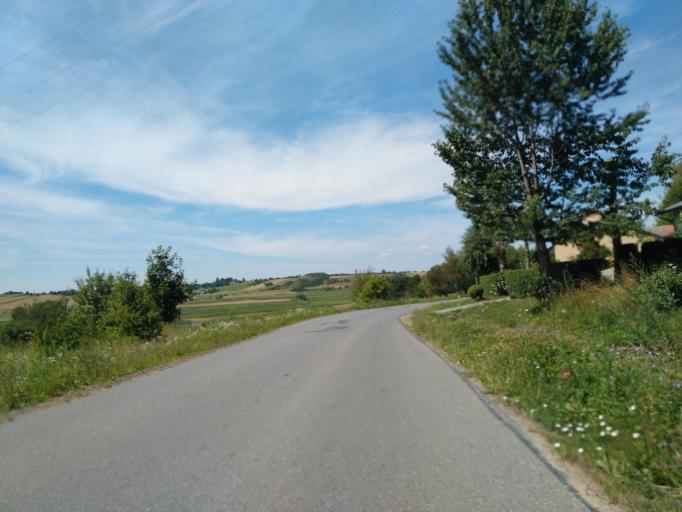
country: PL
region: Subcarpathian Voivodeship
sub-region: Powiat sanocki
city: Nowosielce-Gniewosz
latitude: 49.5422
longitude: 22.1112
